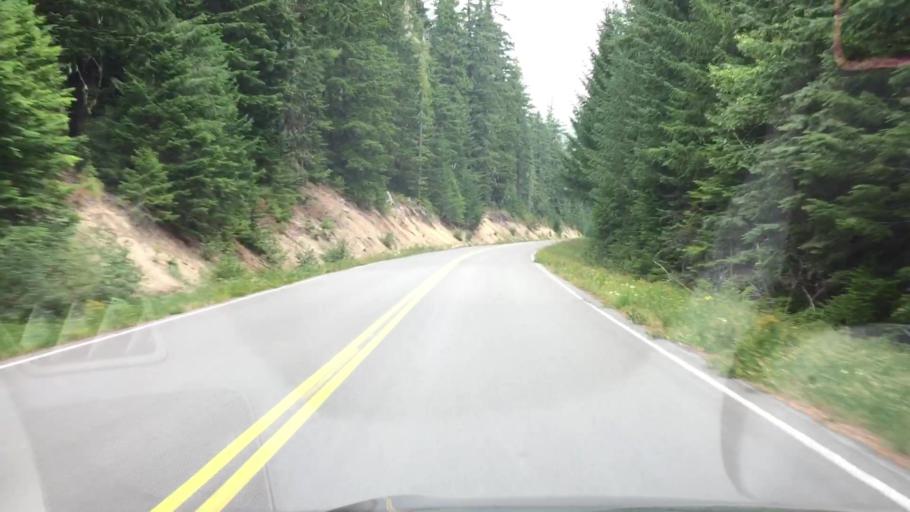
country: US
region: Washington
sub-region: Klickitat County
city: White Salmon
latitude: 46.1184
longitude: -121.6201
